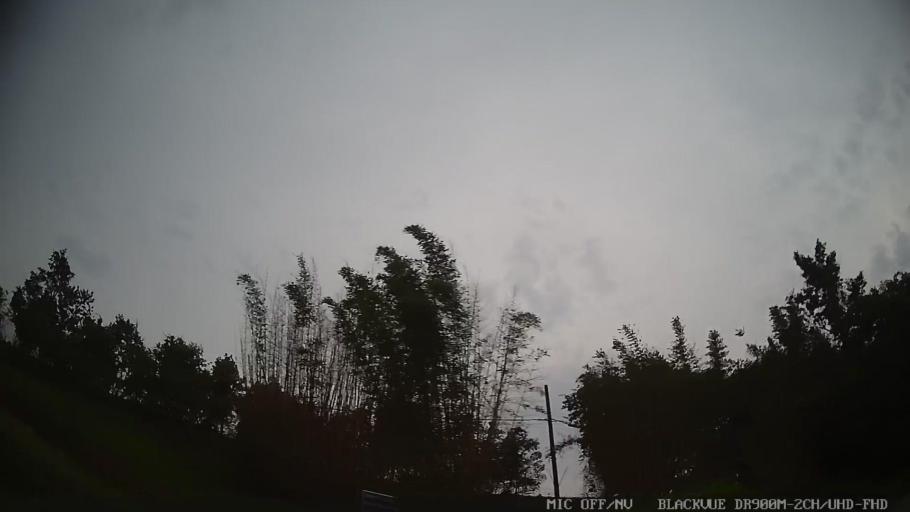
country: BR
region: Sao Paulo
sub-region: Braganca Paulista
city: Braganca Paulista
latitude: -22.9576
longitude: -46.5874
